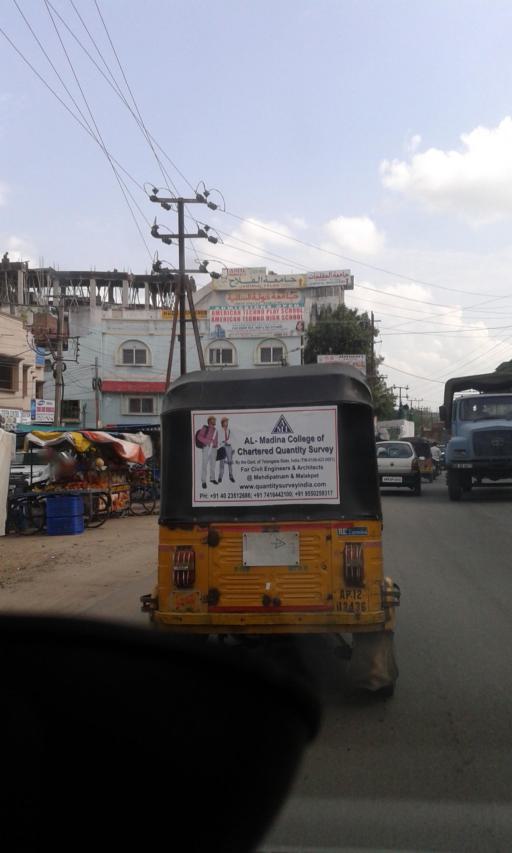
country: IN
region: Telangana
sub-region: Rangareddi
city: Balapur
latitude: 17.3222
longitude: 78.4804
